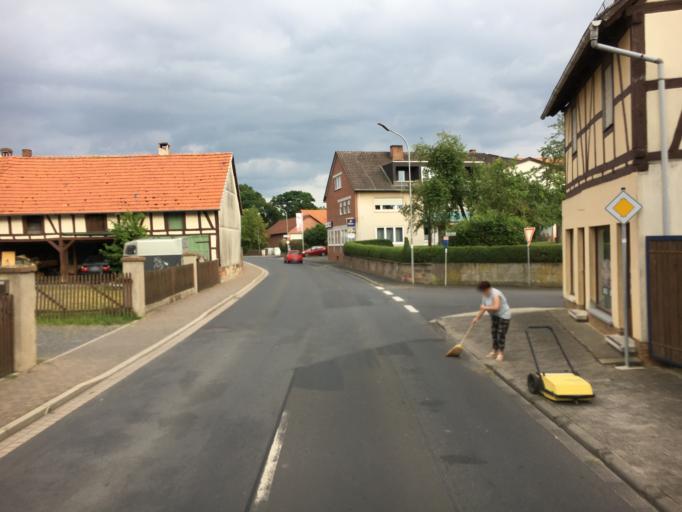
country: DE
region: Hesse
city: Schwalmstadt
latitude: 50.8852
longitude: 9.2526
